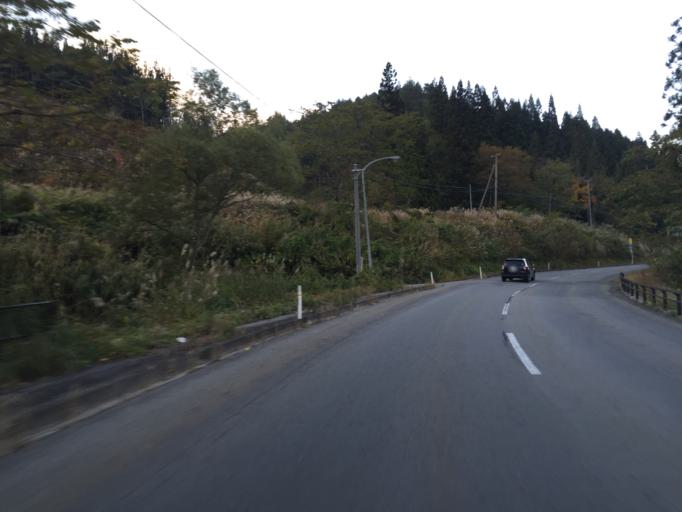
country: JP
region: Yamagata
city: Yonezawa
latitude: 37.8736
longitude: 139.9815
